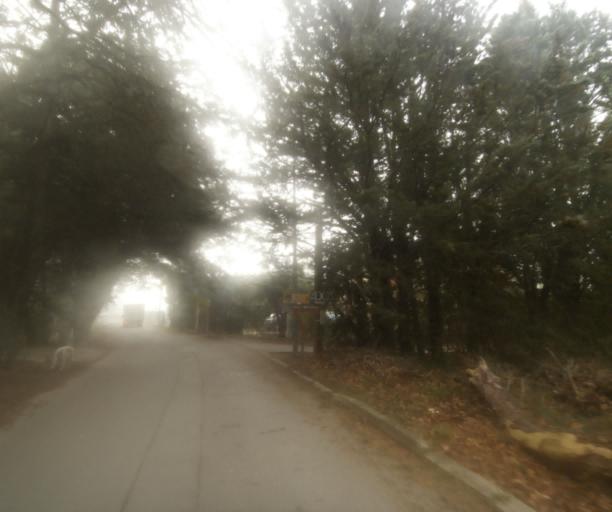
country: FR
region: Provence-Alpes-Cote d'Azur
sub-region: Departement des Bouches-du-Rhone
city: Eguilles
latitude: 43.5446
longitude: 5.3568
